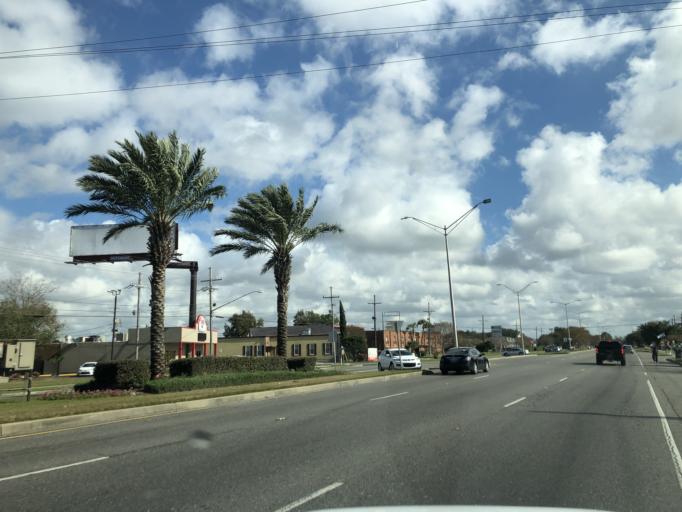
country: US
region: Louisiana
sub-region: Jefferson Parish
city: Kenner
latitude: 30.0051
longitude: -90.2192
